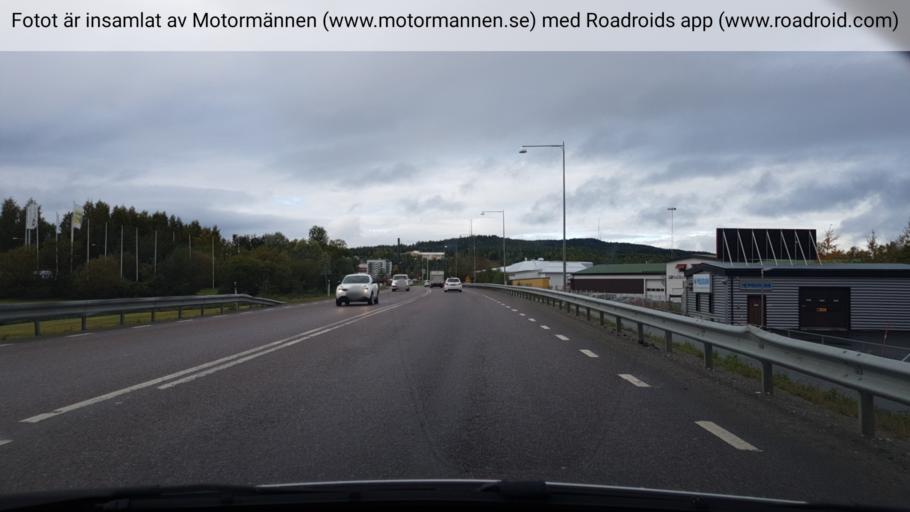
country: SE
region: Vaesternorrland
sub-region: OErnskoeldsviks Kommun
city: Ornskoldsvik
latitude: 63.3038
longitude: 18.7323
